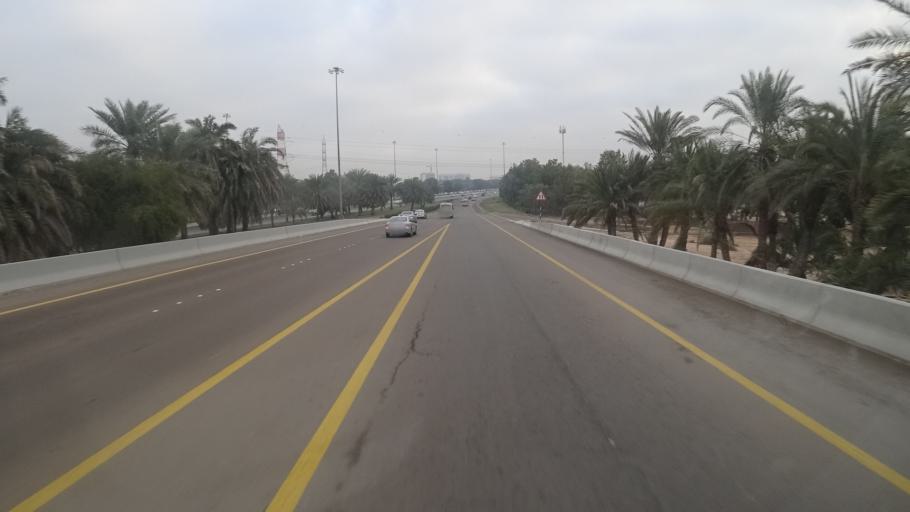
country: AE
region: Abu Dhabi
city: Abu Dhabi
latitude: 24.3911
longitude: 54.5464
